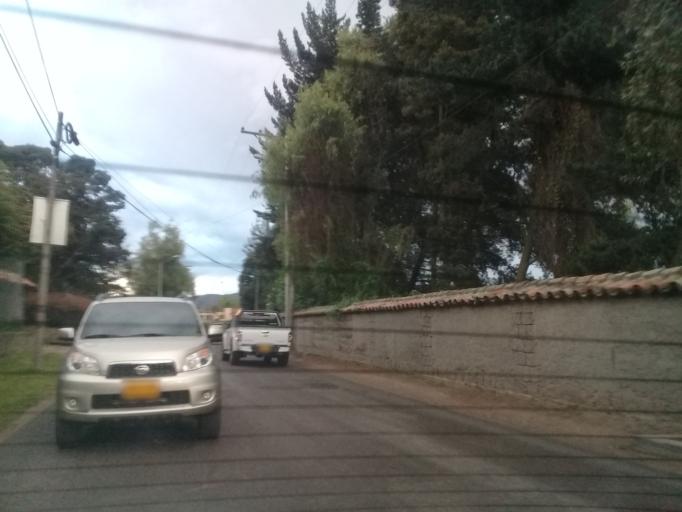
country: CO
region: Cundinamarca
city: Cajica
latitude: 4.9274
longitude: -74.0492
